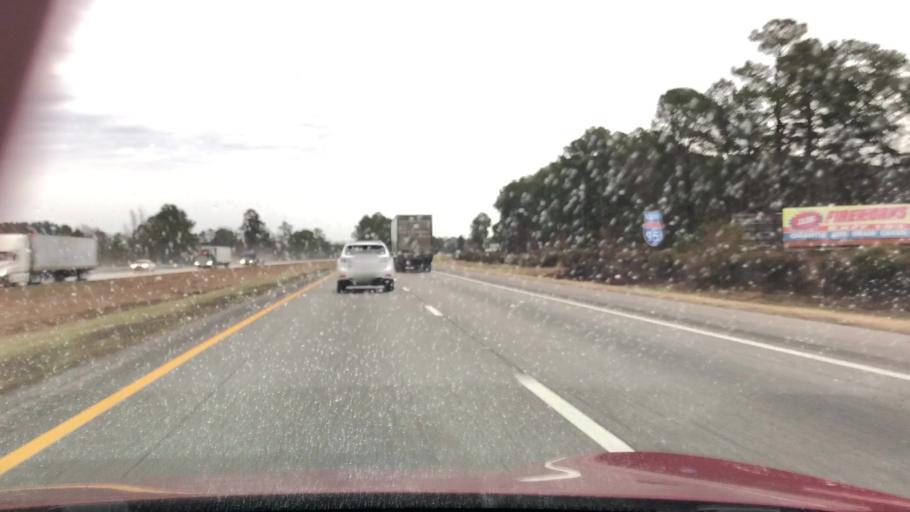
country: US
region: South Carolina
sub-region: Dillon County
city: Latta
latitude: 34.3485
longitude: -79.5262
